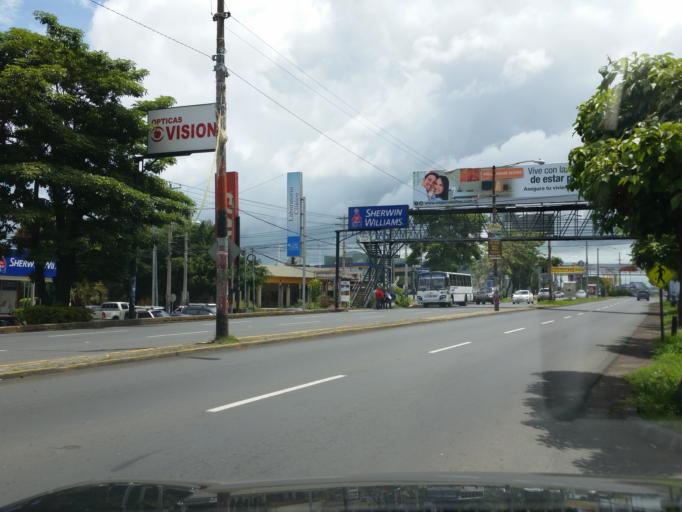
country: NI
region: Managua
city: Managua
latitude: 12.1167
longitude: -86.2584
